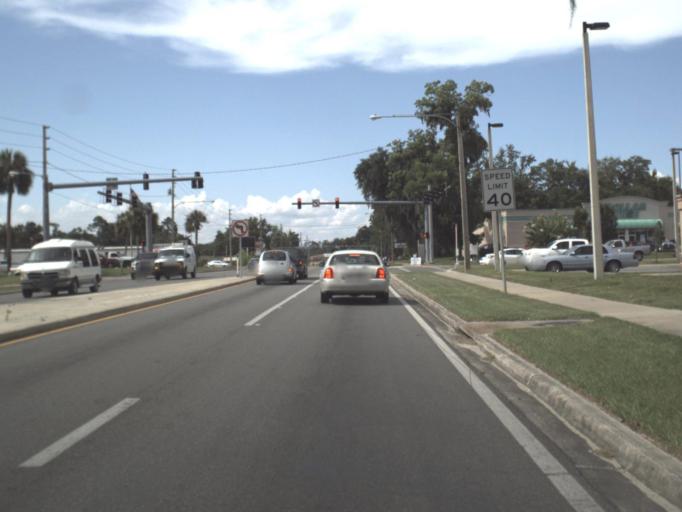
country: US
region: Florida
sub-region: Taylor County
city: Perry
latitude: 30.1024
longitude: -83.5827
